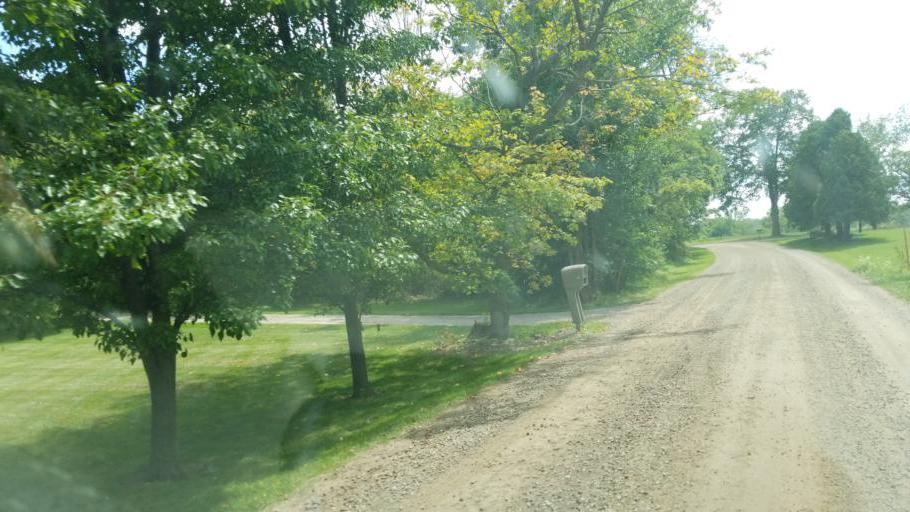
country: US
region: Ohio
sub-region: Knox County
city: Mount Vernon
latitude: 40.3724
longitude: -82.5998
